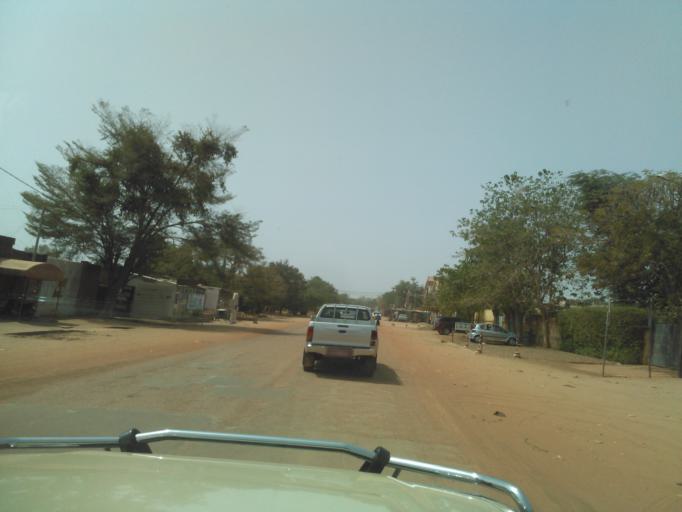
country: BF
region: Centre
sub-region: Kadiogo Province
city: Ouagadougou
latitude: 12.3823
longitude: -1.4849
